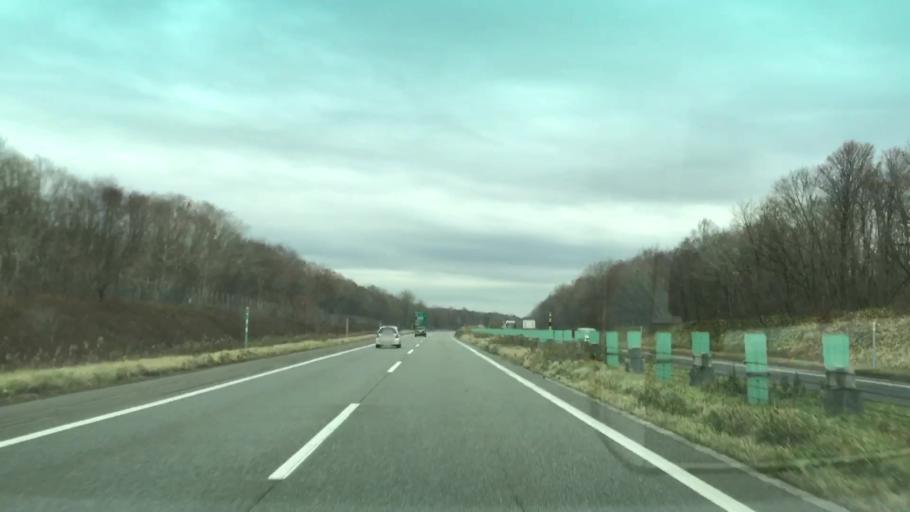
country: JP
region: Hokkaido
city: Chitose
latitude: 42.8024
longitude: 141.6250
